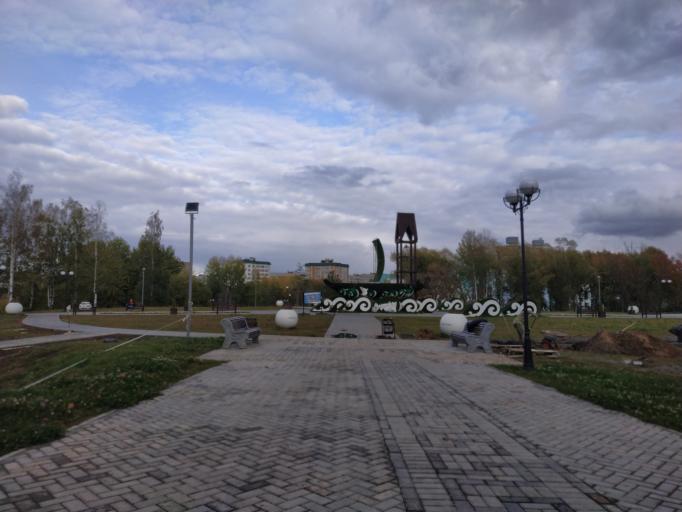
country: RU
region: Chuvashia
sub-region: Cheboksarskiy Rayon
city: Cheboksary
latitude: 56.1479
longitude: 47.2087
